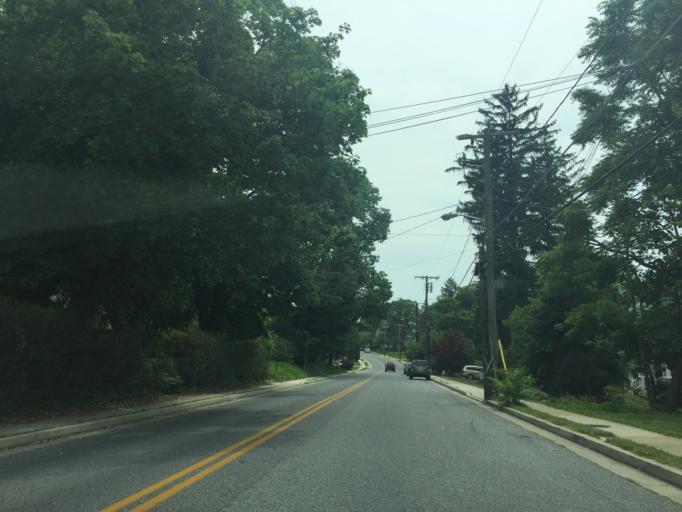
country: US
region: Maryland
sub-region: Baltimore County
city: Towson
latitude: 39.4030
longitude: -76.6142
